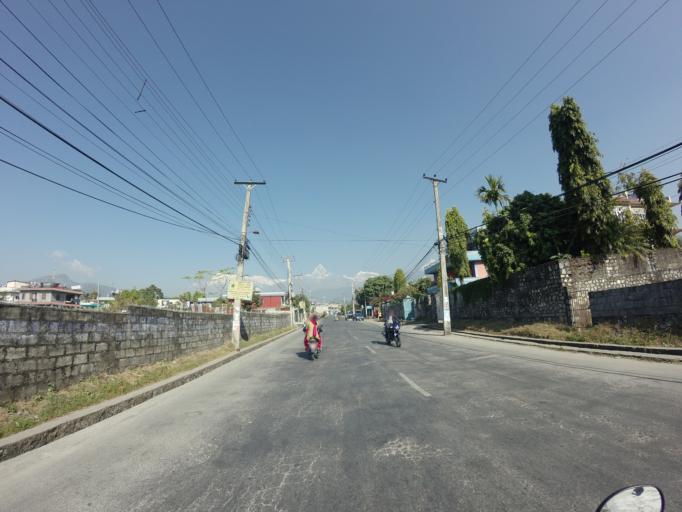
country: NP
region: Western Region
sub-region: Gandaki Zone
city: Pokhara
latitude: 28.2168
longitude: 83.9978
